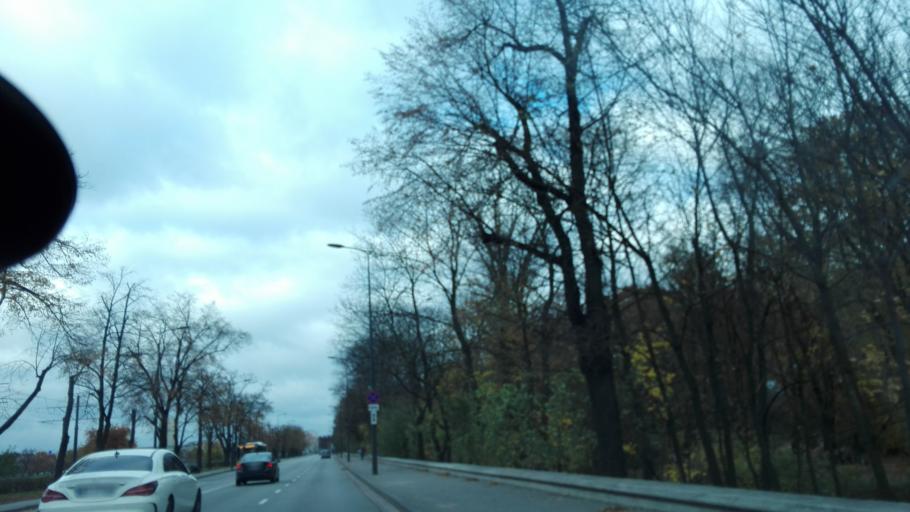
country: PL
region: Masovian Voivodeship
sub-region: Warszawa
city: Praga Polnoc
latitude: 52.2420
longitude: 21.0498
